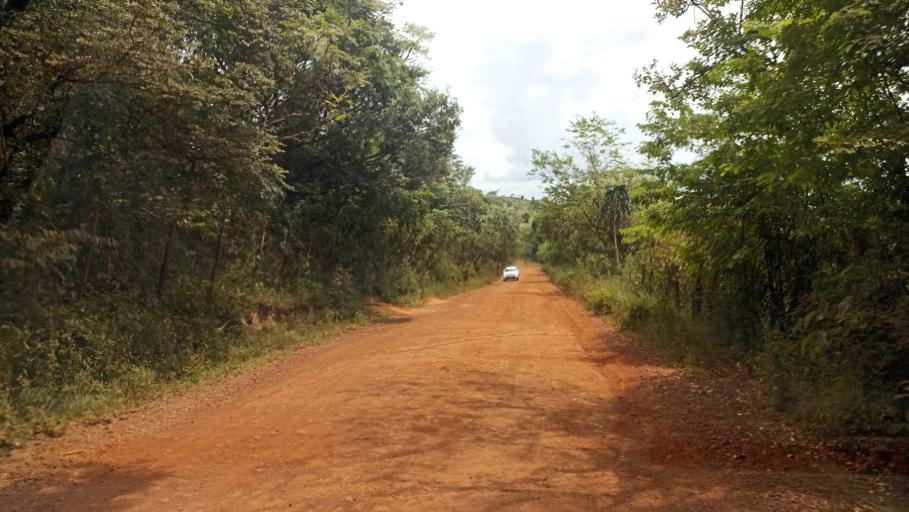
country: BR
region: Minas Gerais
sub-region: Itabirito
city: Itabirito
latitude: -20.3496
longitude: -43.7408
